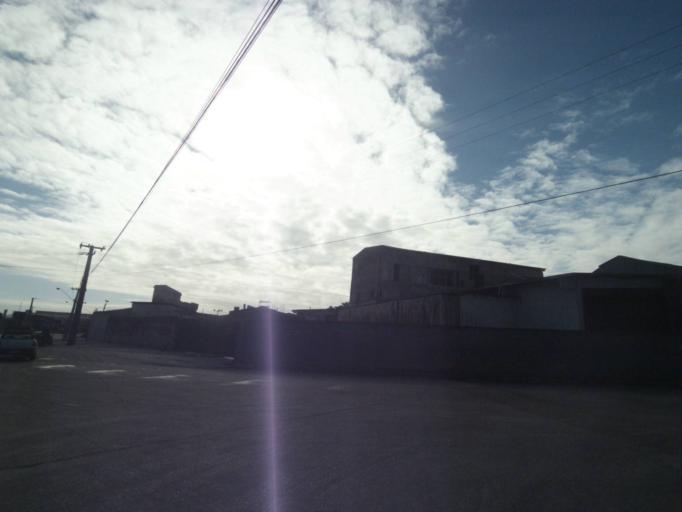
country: BR
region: Parana
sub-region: Paranagua
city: Paranagua
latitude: -25.5160
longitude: -48.5254
